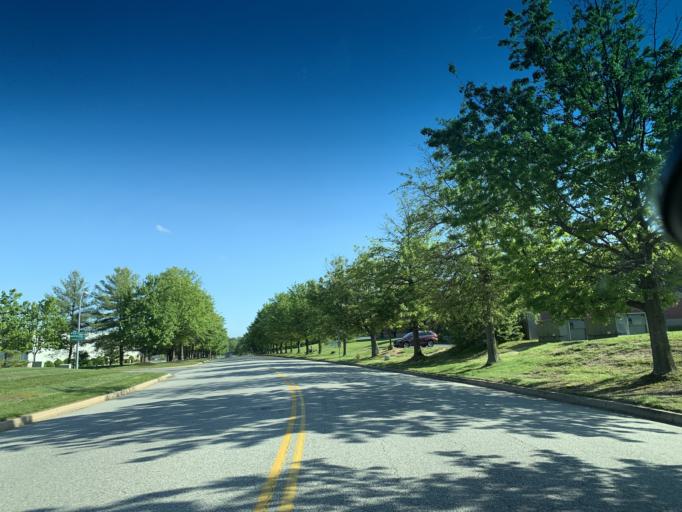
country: US
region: Maryland
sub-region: Harford County
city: Riverside
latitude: 39.4841
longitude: -76.2350
